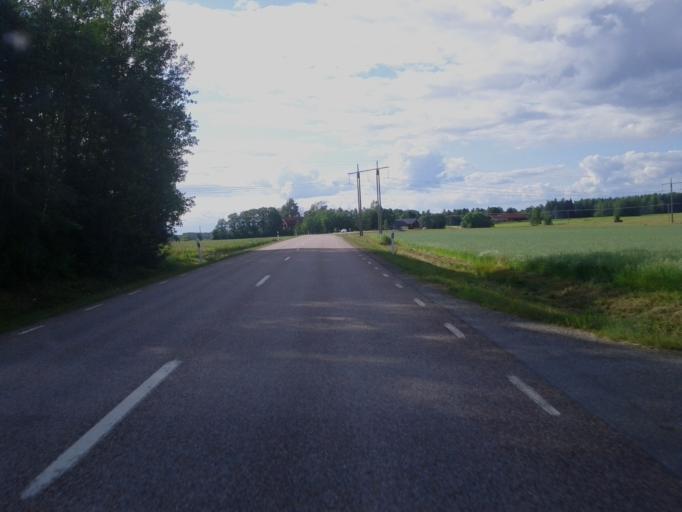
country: SE
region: Vaestmanland
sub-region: Sala Kommun
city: Sala
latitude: 59.9110
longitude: 16.5240
